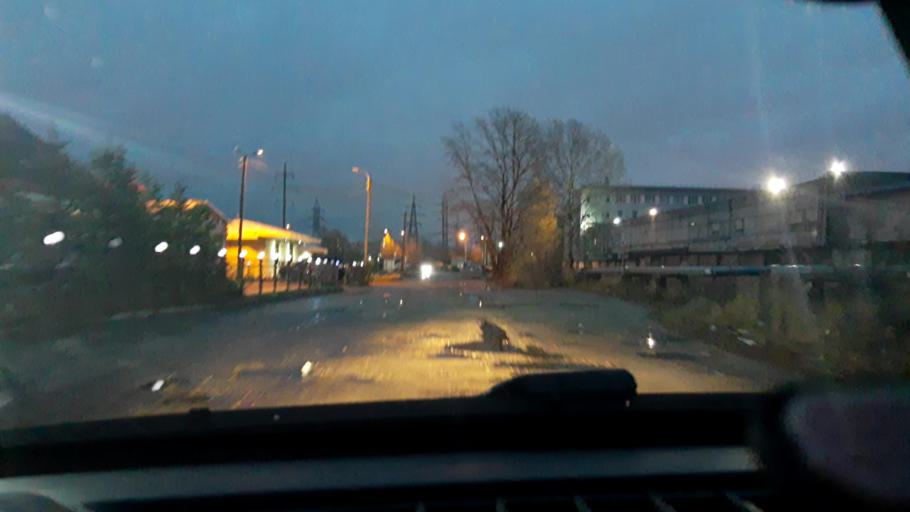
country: RU
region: Nizjnij Novgorod
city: Neklyudovo
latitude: 56.3447
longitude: 43.8849
